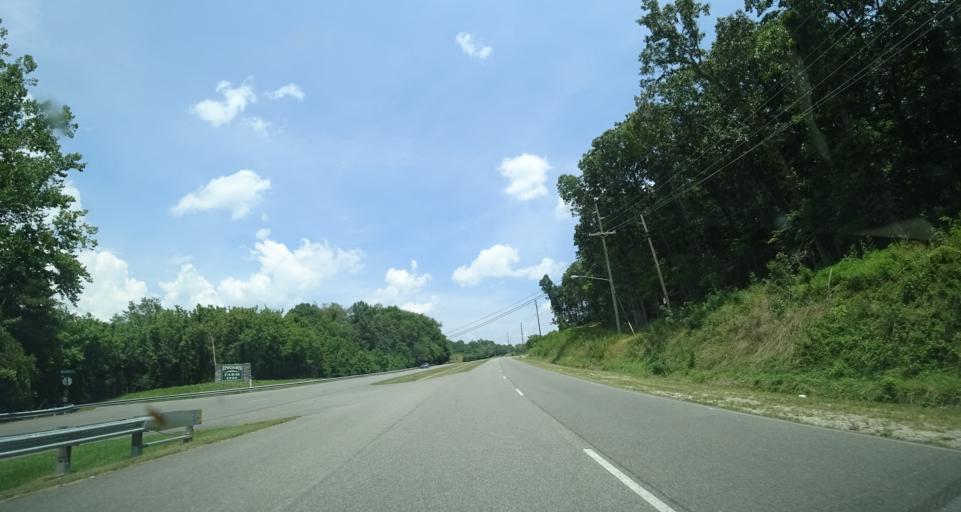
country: US
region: Virginia
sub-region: City of Radford
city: Radford
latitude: 37.1009
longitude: -80.5822
